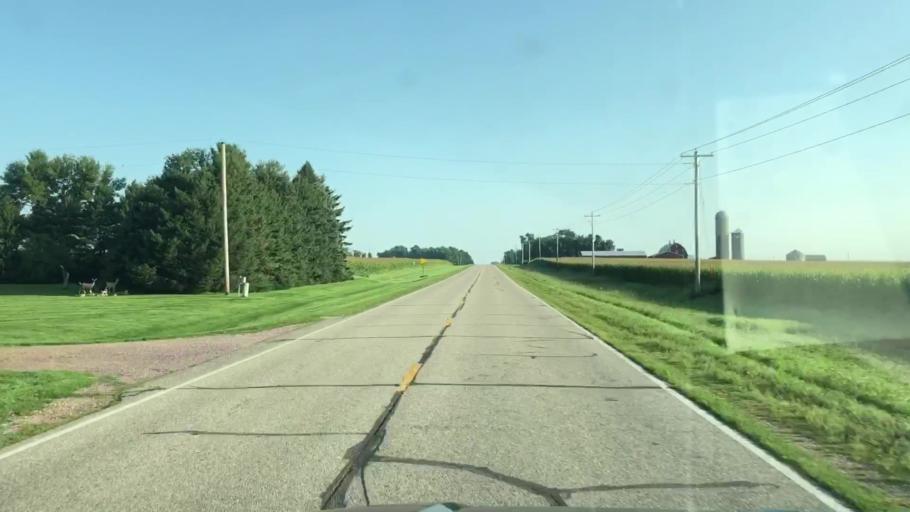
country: US
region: Iowa
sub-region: Lyon County
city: George
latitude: 43.3690
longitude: -95.9983
